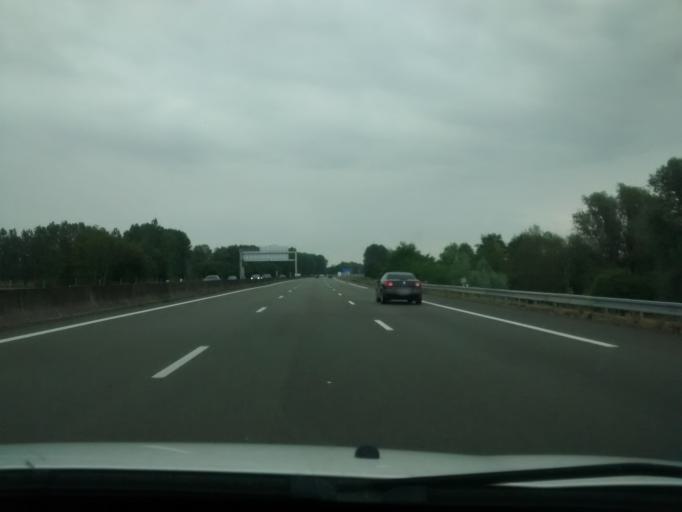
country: FR
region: Pays de la Loire
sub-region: Departement de la Sarthe
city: Champagne
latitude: 48.0521
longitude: 0.3166
